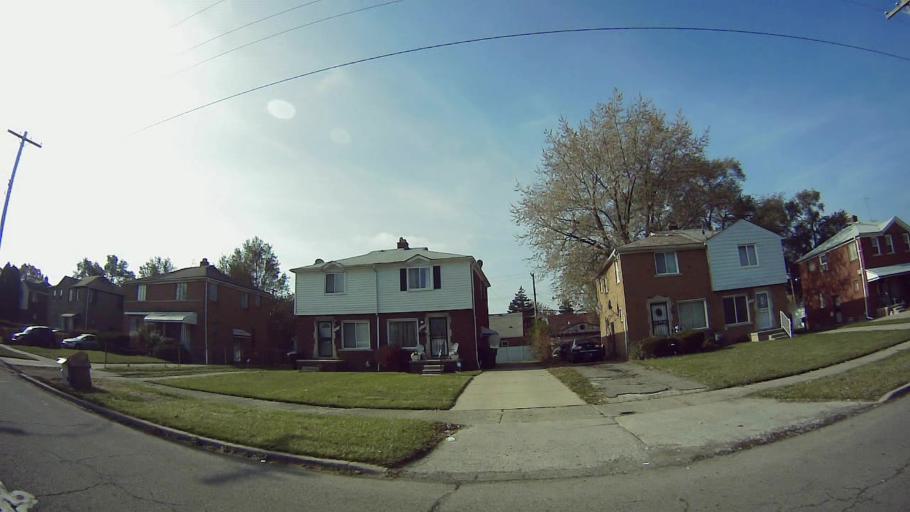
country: US
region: Michigan
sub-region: Oakland County
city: Oak Park
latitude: 42.4287
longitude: -83.1804
